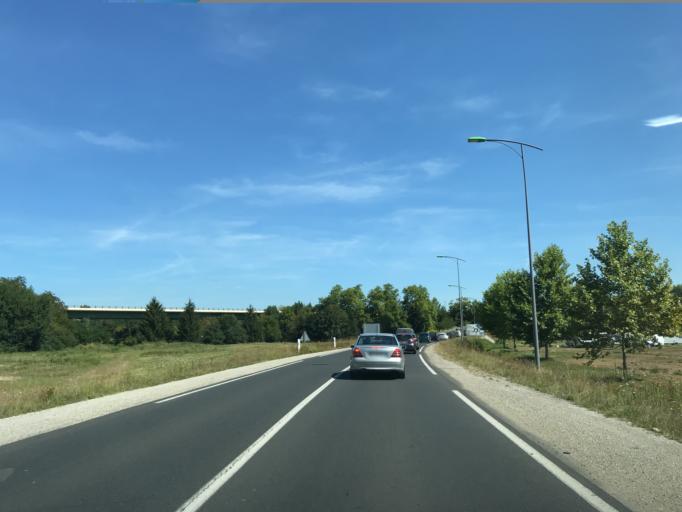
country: FR
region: Limousin
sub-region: Departement de la Correze
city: Saint-Pantaleon-de-Larche
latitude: 45.1658
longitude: 1.4652
